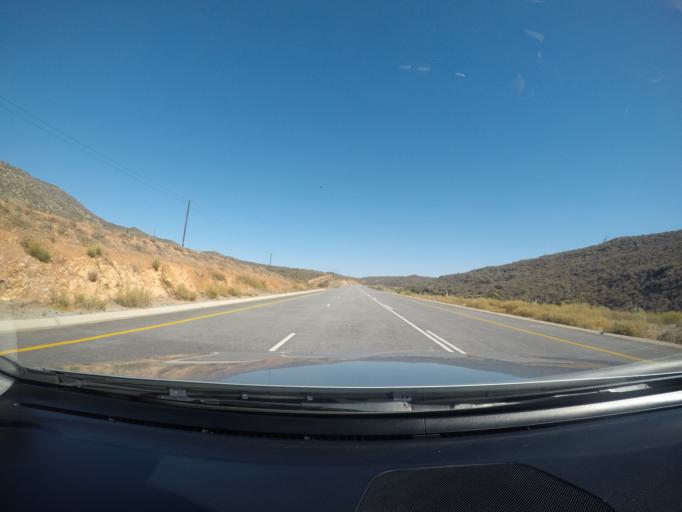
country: ZA
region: Western Cape
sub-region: West Coast District Municipality
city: Clanwilliam
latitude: -32.3434
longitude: 18.9264
